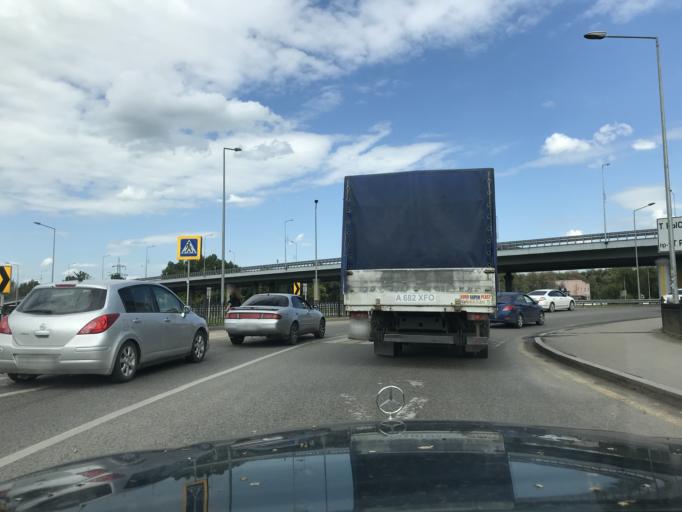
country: KZ
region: Almaty Qalasy
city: Almaty
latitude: 43.3027
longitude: 76.8946
